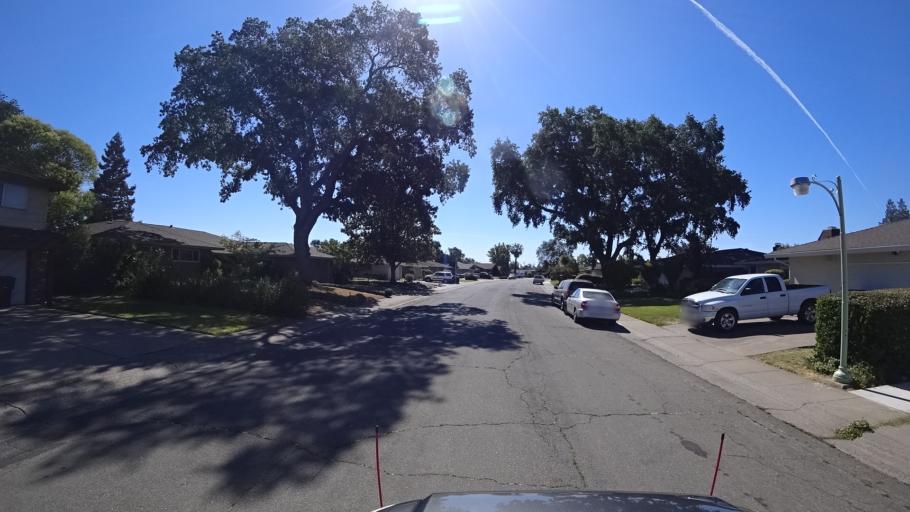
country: US
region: California
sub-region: Sacramento County
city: Parkway
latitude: 38.4989
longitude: -121.5125
